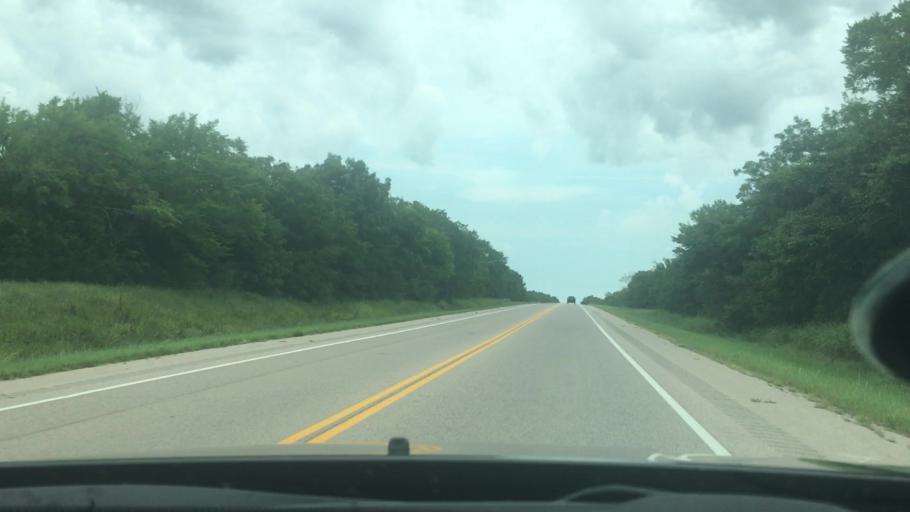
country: US
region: Oklahoma
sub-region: Seminole County
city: Konawa
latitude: 34.9579
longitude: -96.6786
